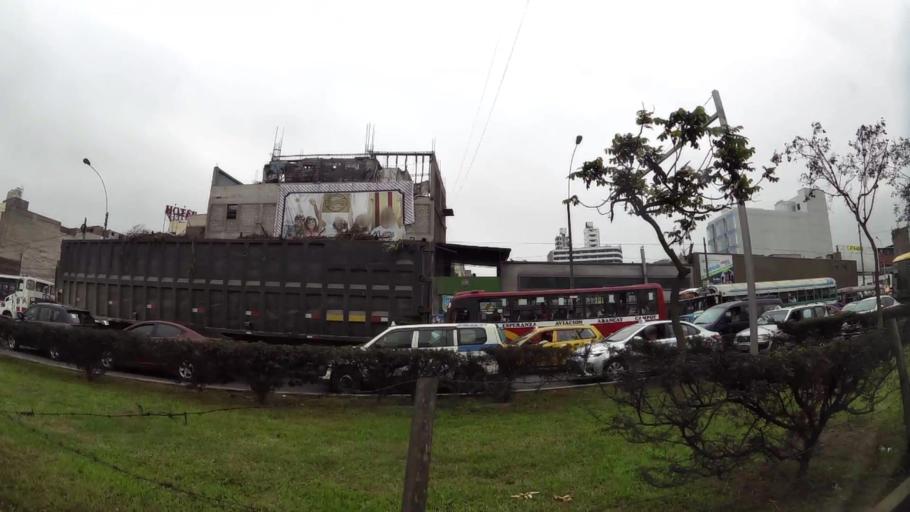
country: PE
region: Lima
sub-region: Lima
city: San Luis
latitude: -12.0726
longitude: -77.0133
